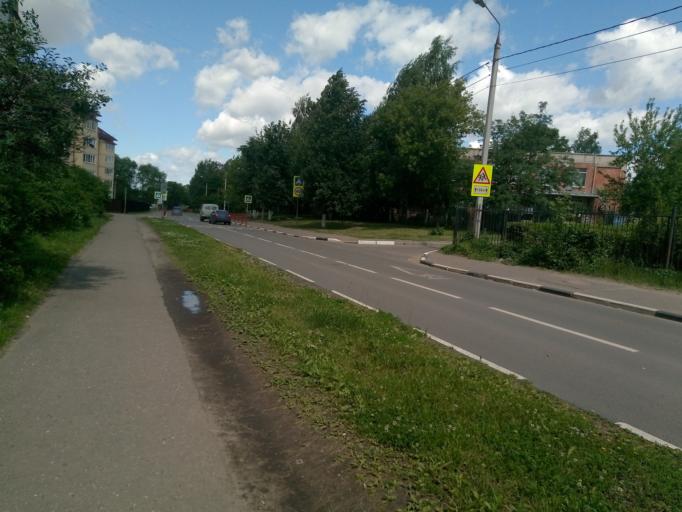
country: RU
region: Jaroslavl
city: Yaroslavl
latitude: 57.6568
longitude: 39.9571
